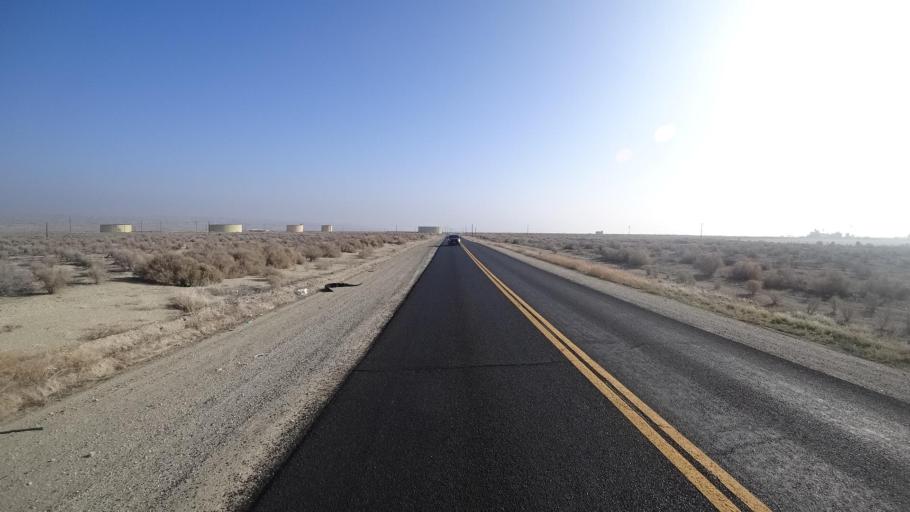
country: US
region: California
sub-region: Kern County
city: Taft Heights
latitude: 35.1803
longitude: -119.5219
